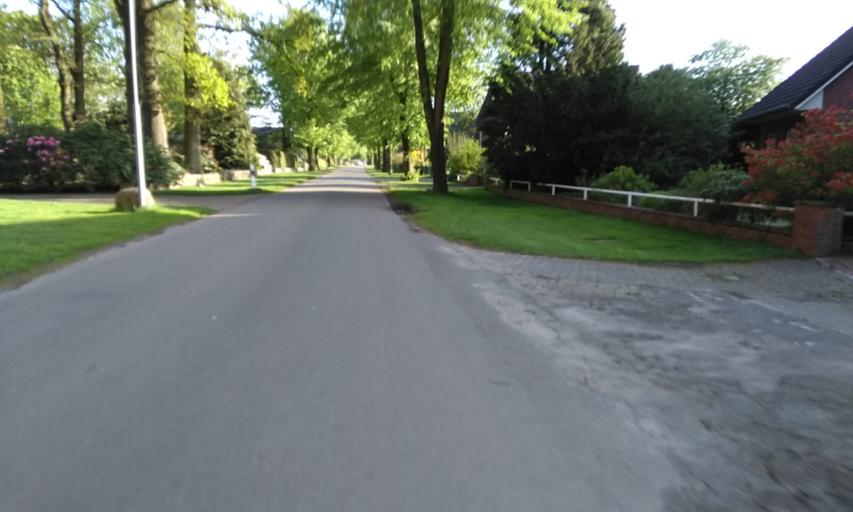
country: DE
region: Lower Saxony
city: Harsefeld
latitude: 53.4184
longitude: 9.5511
